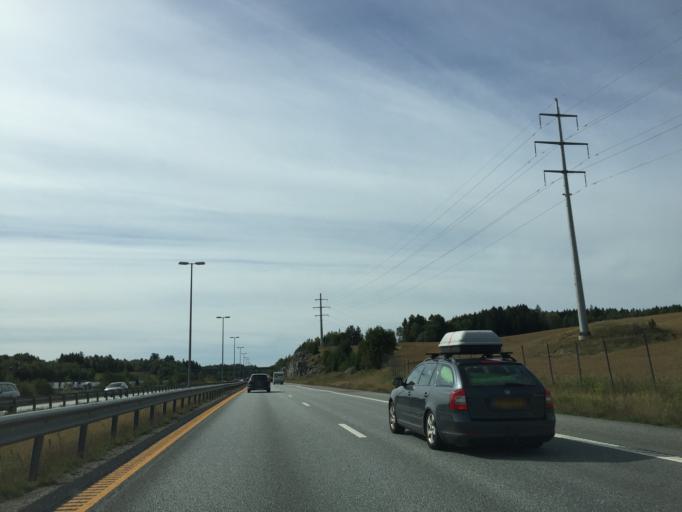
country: NO
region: Akershus
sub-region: Vestby
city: Vestby
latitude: 59.5893
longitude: 10.7367
